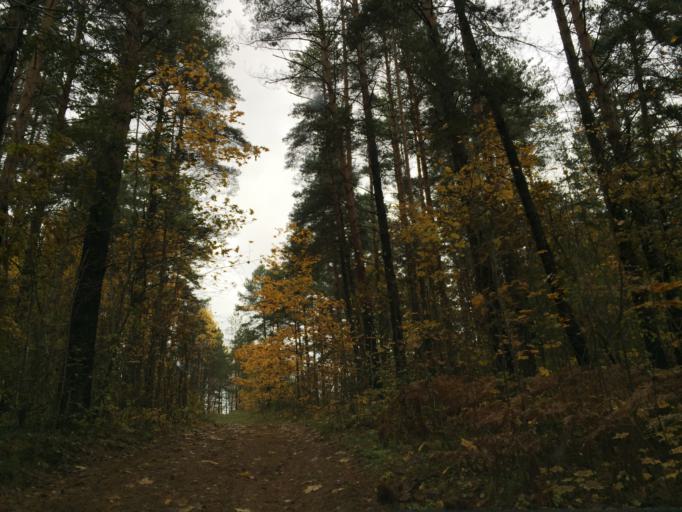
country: LV
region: Ogre
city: Ogre
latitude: 56.7968
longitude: 24.6429
